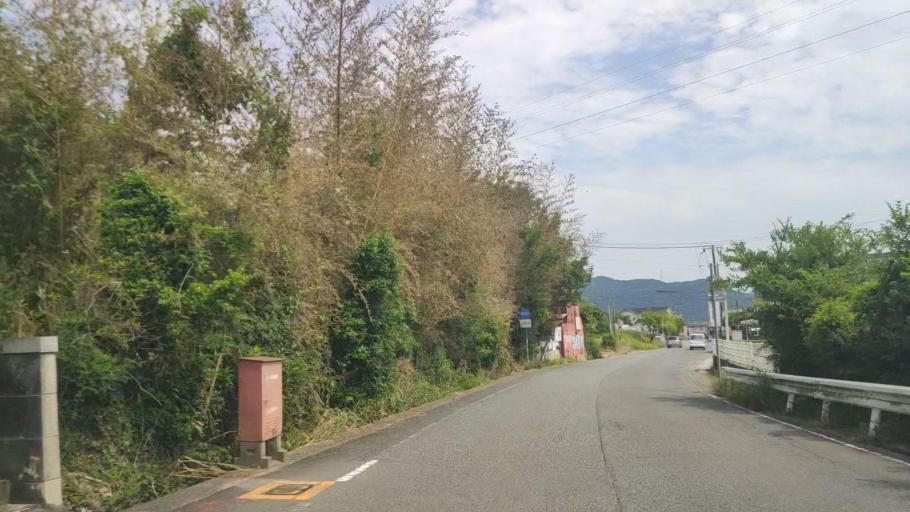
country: JP
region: Hyogo
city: Tatsunocho-tominaga
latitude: 34.8383
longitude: 134.6016
